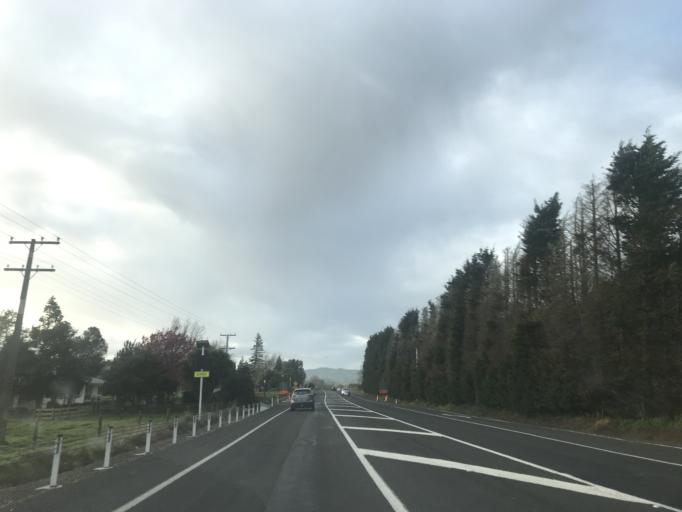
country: NZ
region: Waikato
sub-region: Hauraki District
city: Waihi
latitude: -37.4293
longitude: 175.8711
